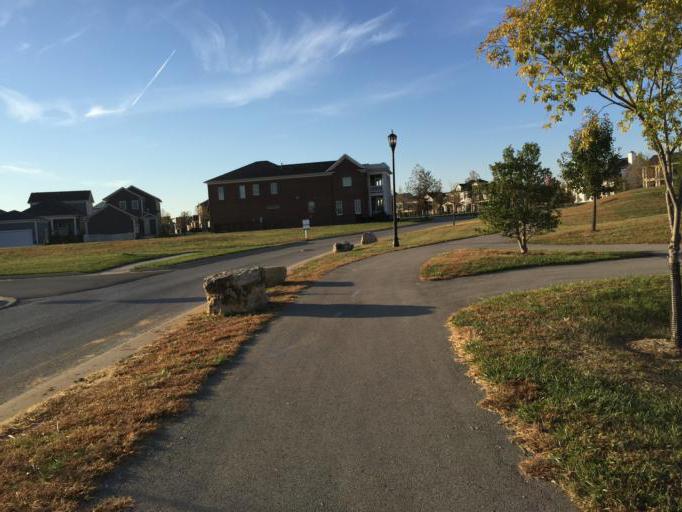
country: US
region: Kentucky
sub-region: Jefferson County
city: Worthington
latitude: 38.3287
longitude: -85.5663
